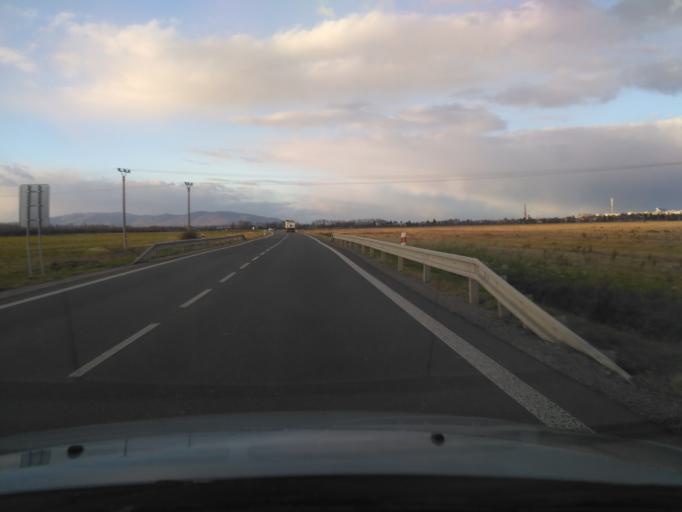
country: SK
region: Kosicky
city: Trebisov
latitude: 48.6113
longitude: 21.7078
